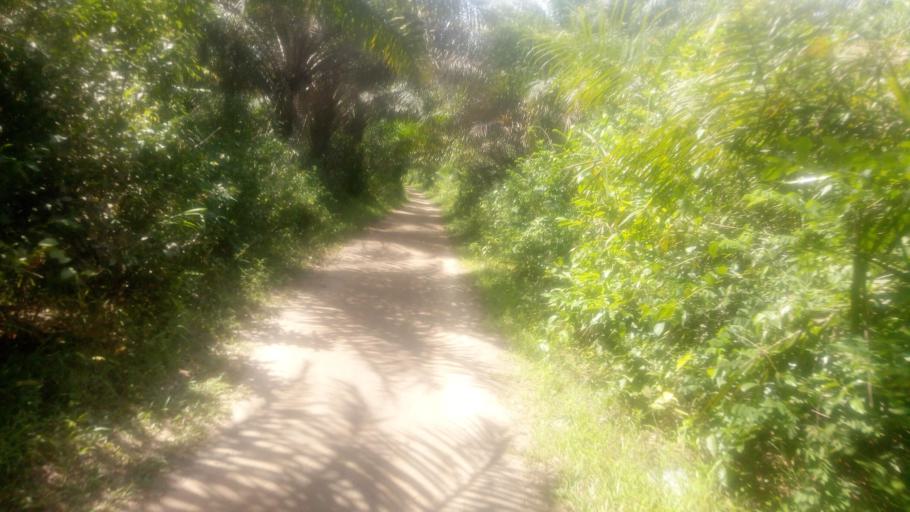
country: SL
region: Northern Province
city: Magburaka
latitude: 8.6571
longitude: -12.0691
